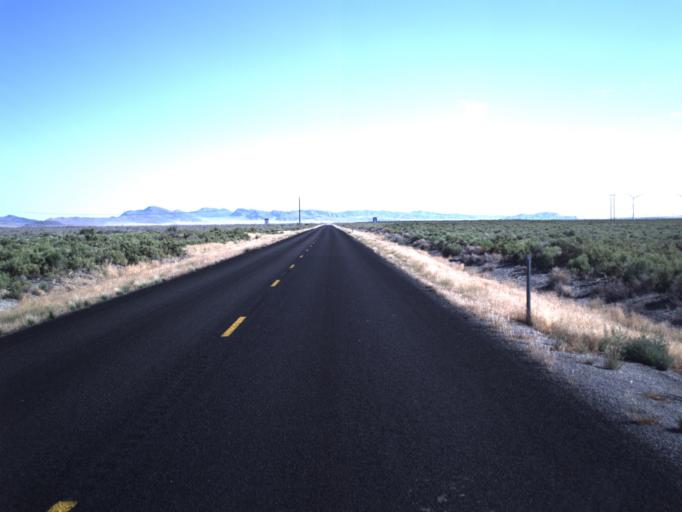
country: US
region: Utah
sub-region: Beaver County
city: Milford
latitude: 38.5639
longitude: -112.9906
